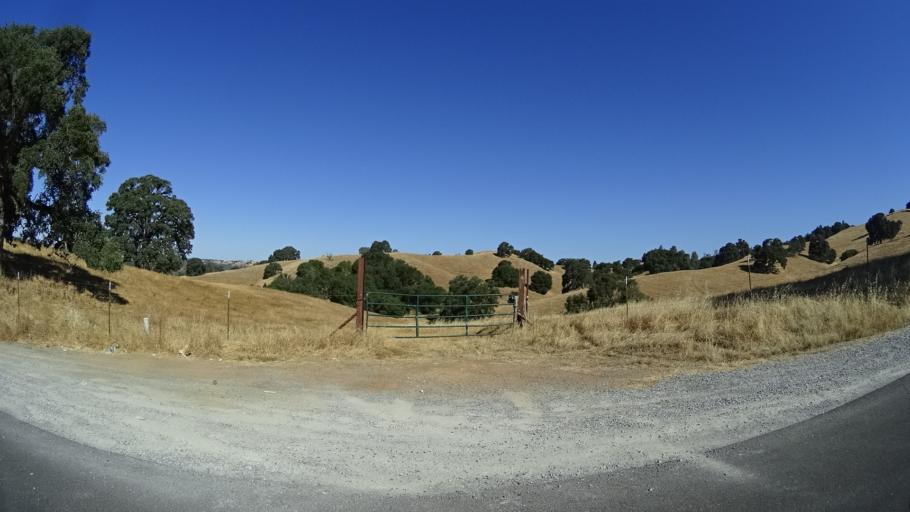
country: US
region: California
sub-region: Calaveras County
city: San Andreas
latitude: 38.2214
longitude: -120.6841
